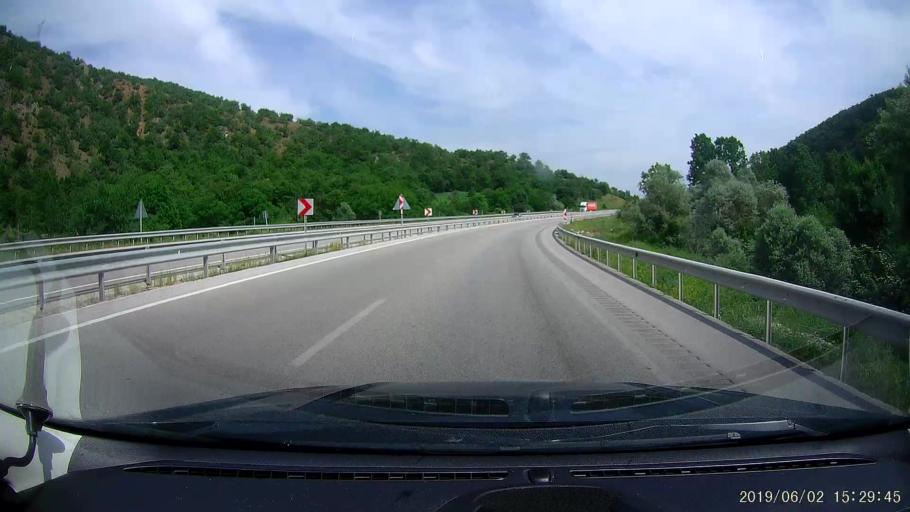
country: TR
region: Amasya
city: Saraycik
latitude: 40.9644
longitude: 35.0959
